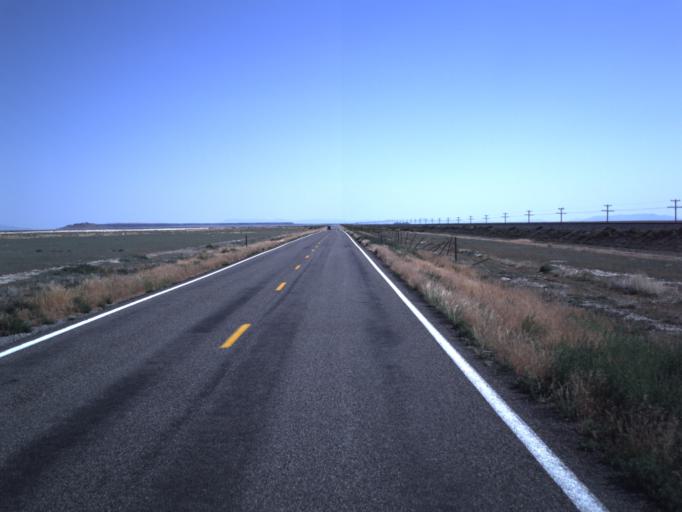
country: US
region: Utah
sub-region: Millard County
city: Delta
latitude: 39.0241
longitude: -112.7780
